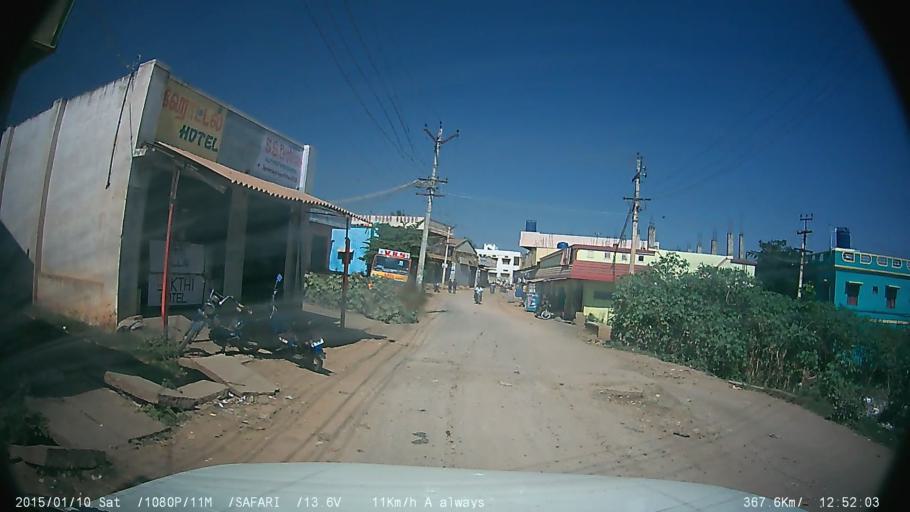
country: IN
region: Tamil Nadu
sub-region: Krishnagiri
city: Hosur
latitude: 12.7749
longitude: 77.7986
